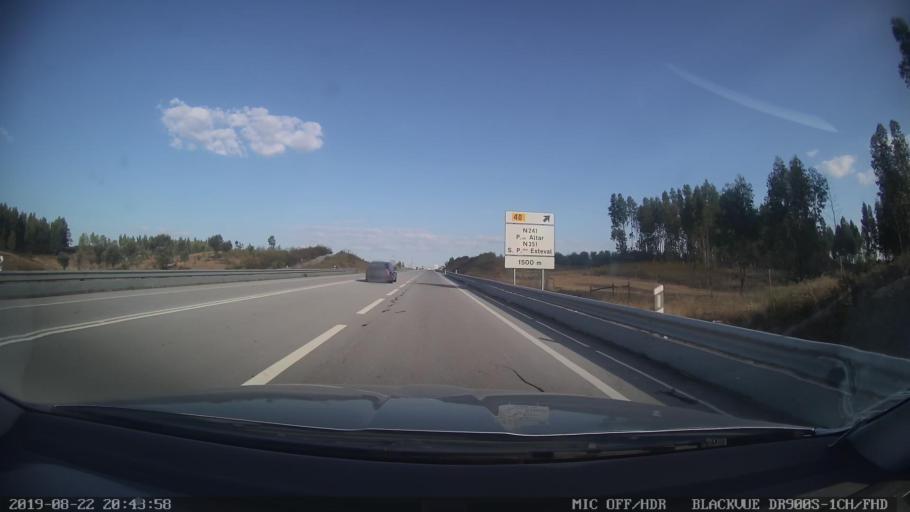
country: PT
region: Castelo Branco
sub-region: Proenca-A-Nova
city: Proenca-a-Nova
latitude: 39.7030
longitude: -7.8424
